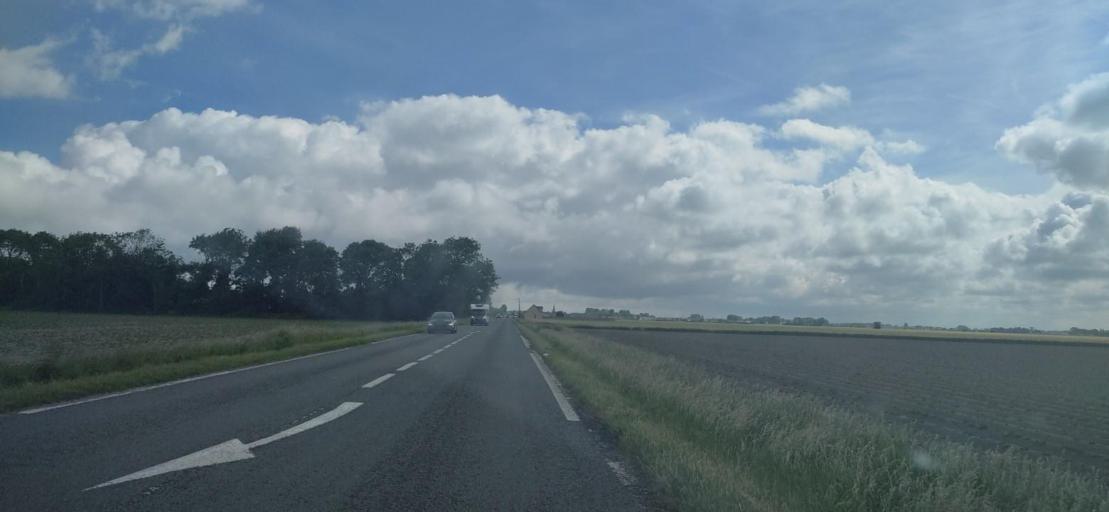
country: FR
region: Nord-Pas-de-Calais
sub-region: Departement du Pas-de-Calais
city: Oye-Plage
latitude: 50.9674
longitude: 2.0141
